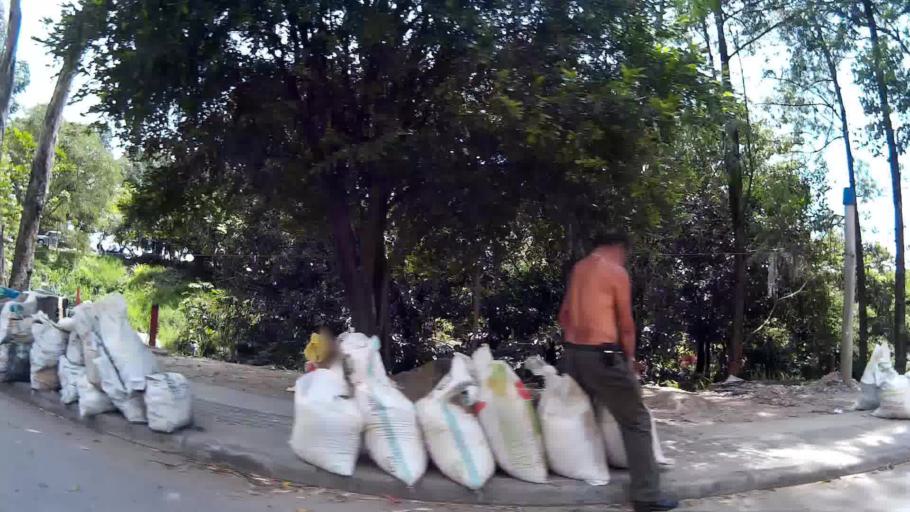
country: CO
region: Antioquia
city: Medellin
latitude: 6.2576
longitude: -75.6269
